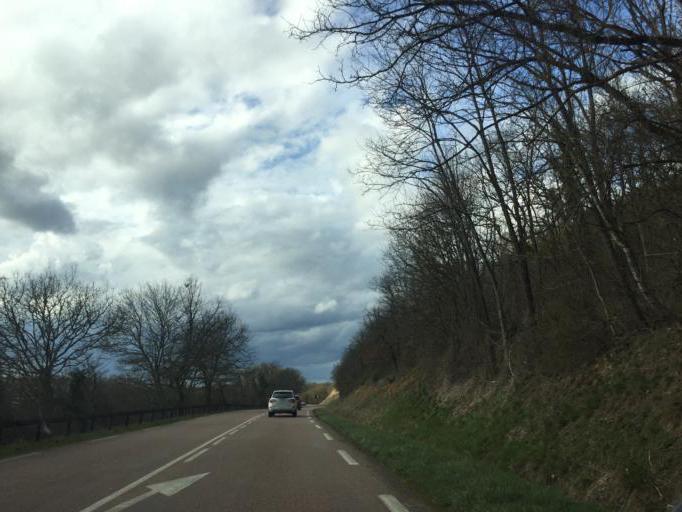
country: FR
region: Bourgogne
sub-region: Departement de la Nievre
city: Clamecy
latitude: 47.4471
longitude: 3.5563
